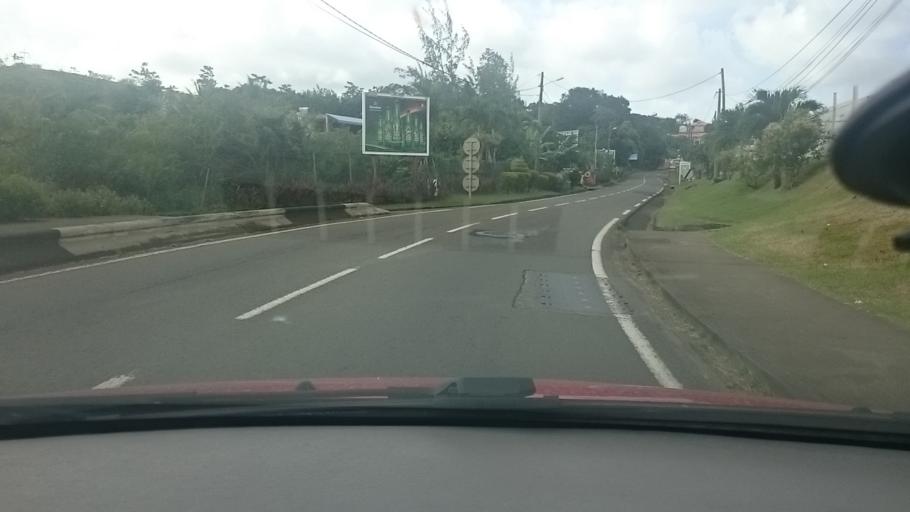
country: MQ
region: Martinique
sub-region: Martinique
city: Saint-Esprit
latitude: 14.5659
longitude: -60.9357
